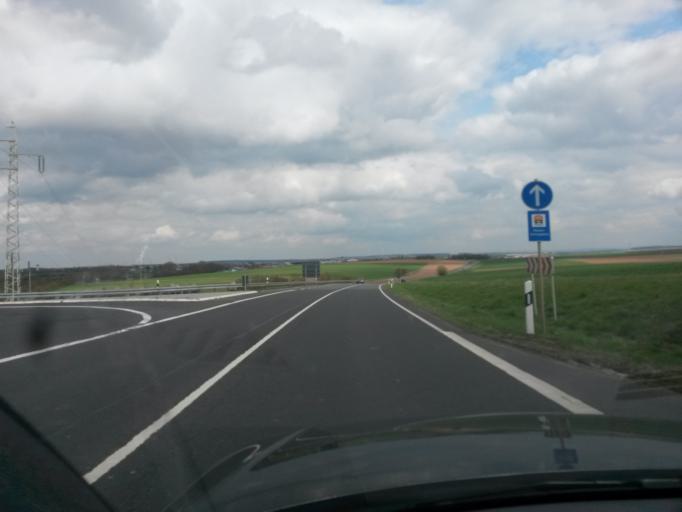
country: DE
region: Bavaria
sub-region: Regierungsbezirk Unterfranken
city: Kurnach
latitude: 49.8565
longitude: 10.0210
